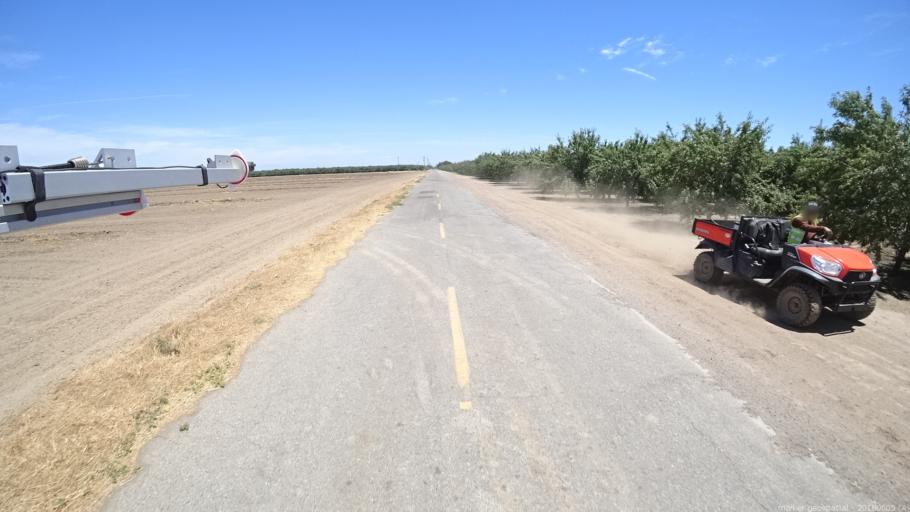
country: US
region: California
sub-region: Madera County
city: Chowchilla
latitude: 37.1055
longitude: -120.3004
